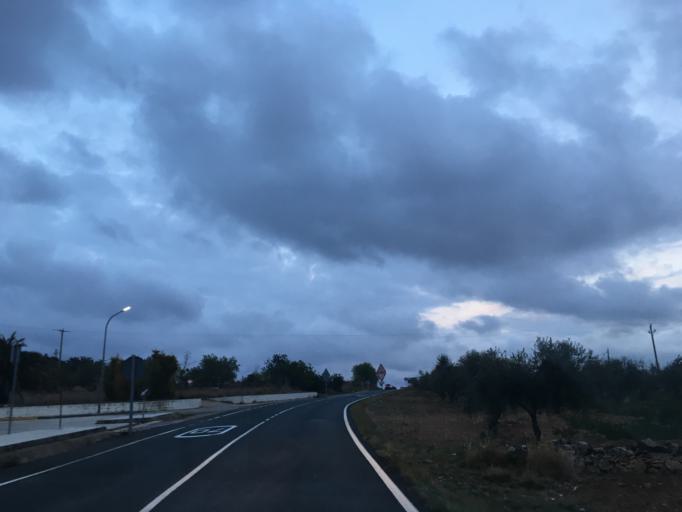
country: ES
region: Catalonia
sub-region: Provincia de Tarragona
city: la Bisbal del Penedes
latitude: 41.2786
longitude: 1.4955
